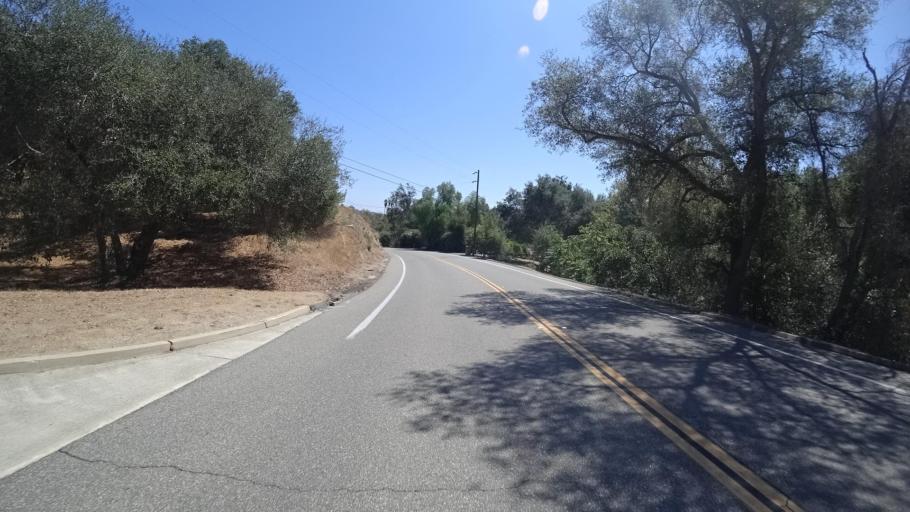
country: US
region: California
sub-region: San Diego County
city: Fallbrook
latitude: 33.3565
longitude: -117.2020
